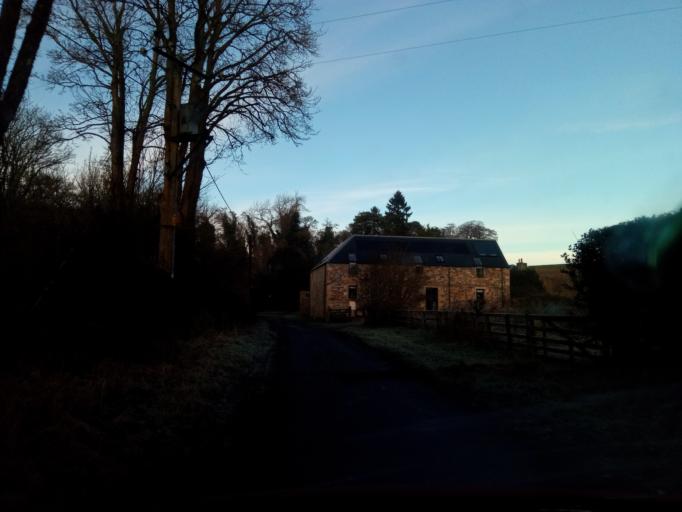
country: GB
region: Scotland
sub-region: The Scottish Borders
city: Hawick
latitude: 55.4573
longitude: -2.7220
